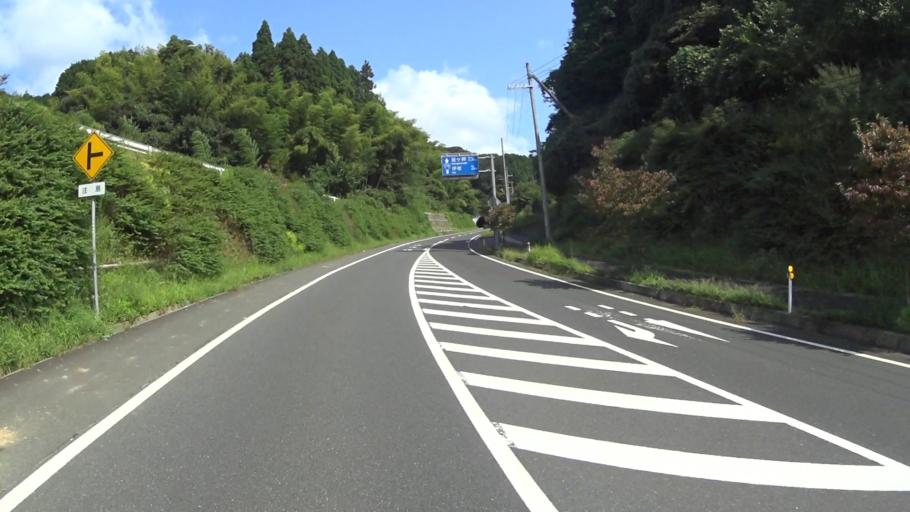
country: JP
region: Kyoto
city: Miyazu
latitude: 35.6590
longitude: 135.2572
